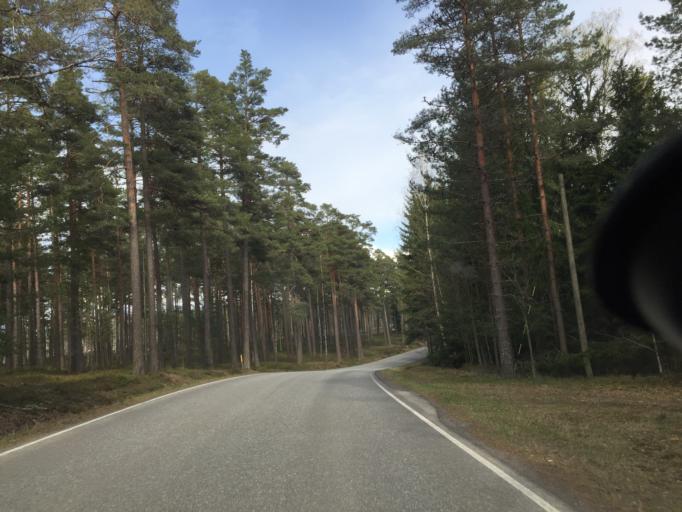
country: FI
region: Varsinais-Suomi
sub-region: Salo
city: Saerkisalo
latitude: 60.0012
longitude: 23.0860
